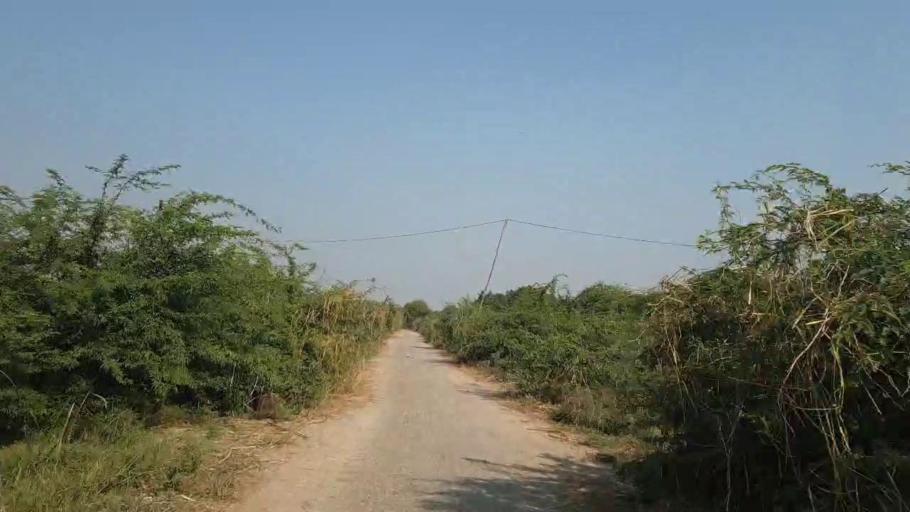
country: PK
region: Sindh
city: Matli
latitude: 25.0012
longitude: 68.6223
